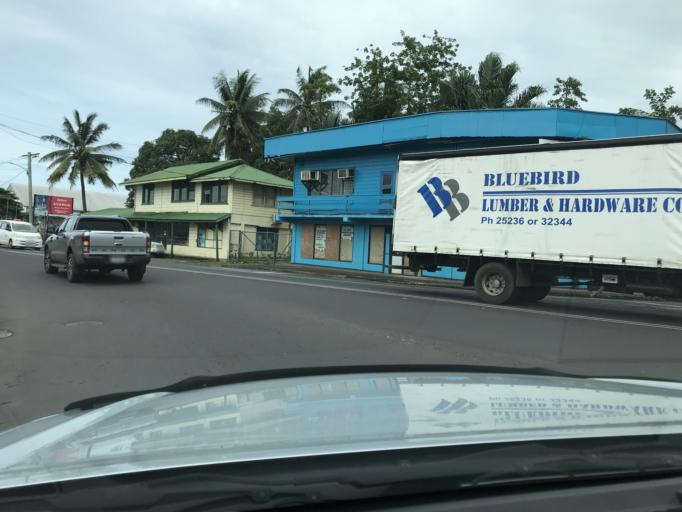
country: WS
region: Tuamasaga
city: Apia
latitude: -13.8383
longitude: -171.7715
